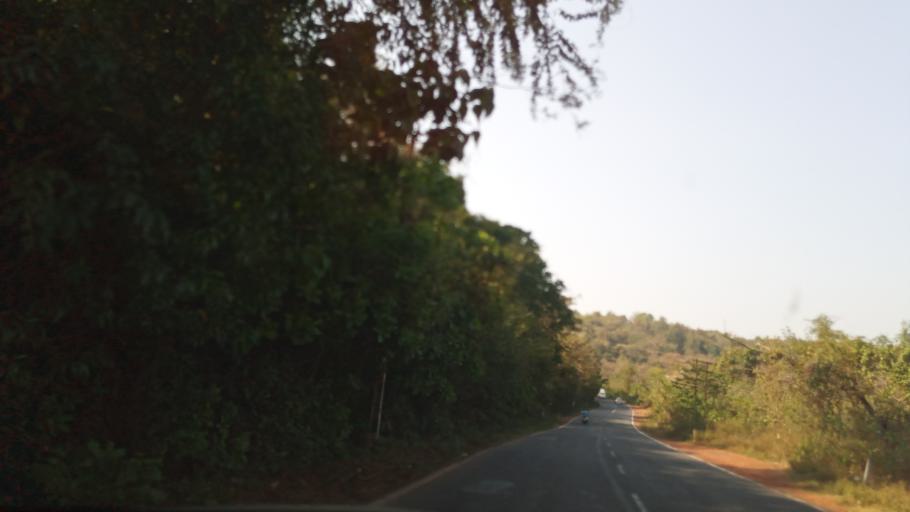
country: IN
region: Goa
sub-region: North Goa
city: Bandora
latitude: 15.4176
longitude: 73.9856
